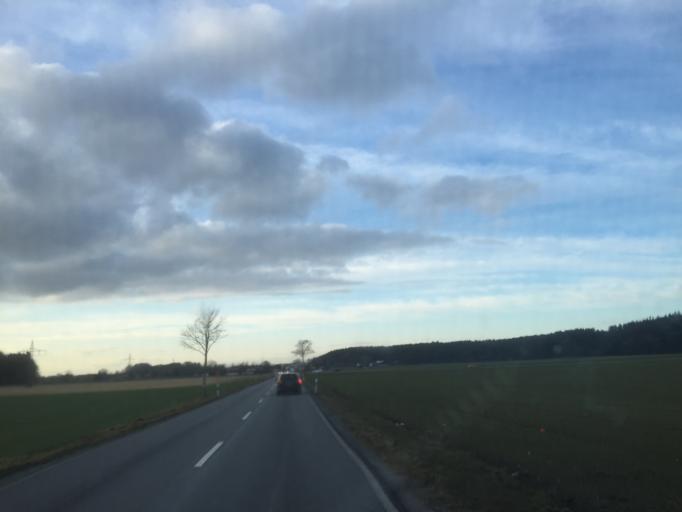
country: DE
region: Bavaria
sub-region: Upper Bavaria
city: Nussdorf
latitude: 47.8824
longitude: 12.5852
